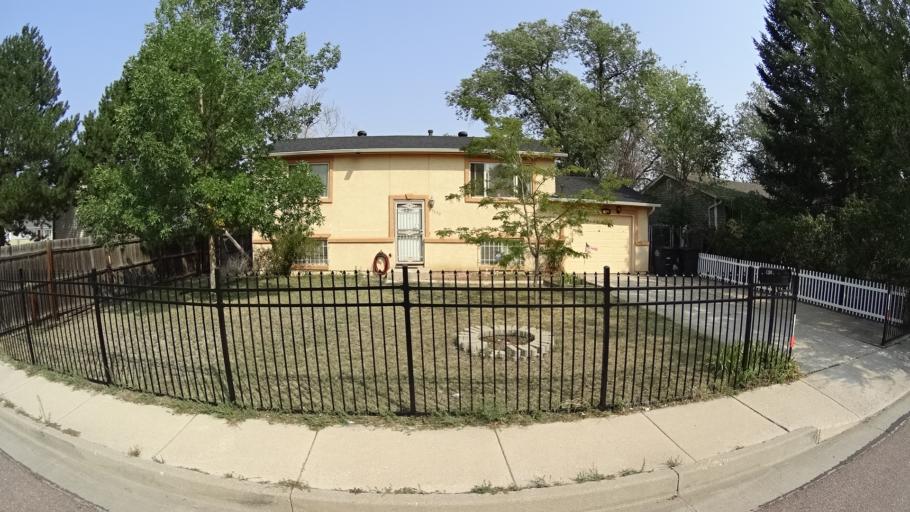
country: US
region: Colorado
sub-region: El Paso County
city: Stratmoor
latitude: 38.8097
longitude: -104.7605
